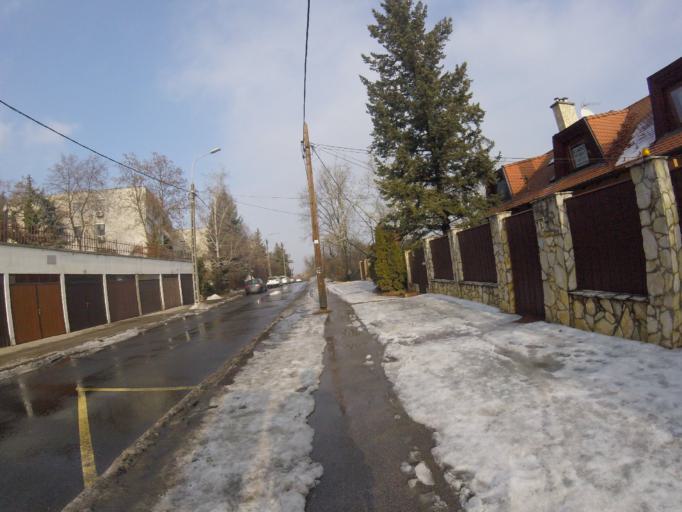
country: HU
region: Budapest
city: Budapest III. keruelet
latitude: 47.5333
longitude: 19.0258
